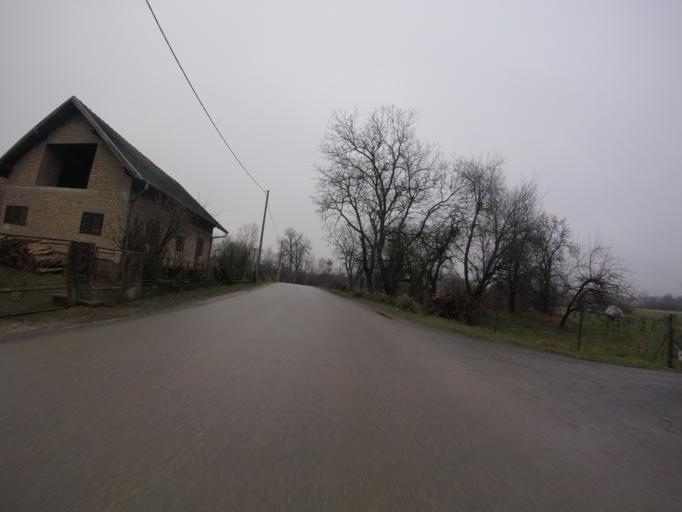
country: HR
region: Sisacko-Moslavacka
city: Lekenik
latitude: 45.6392
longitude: 16.2821
